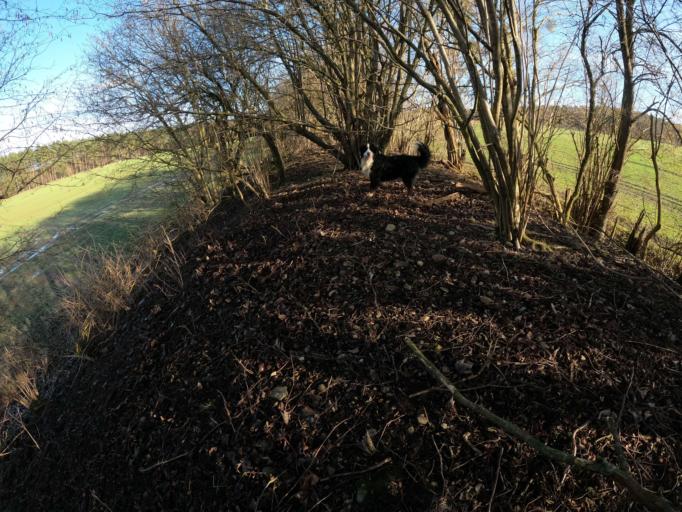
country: PL
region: West Pomeranian Voivodeship
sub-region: Powiat koszalinski
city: Polanow
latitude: 54.2152
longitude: 16.7353
